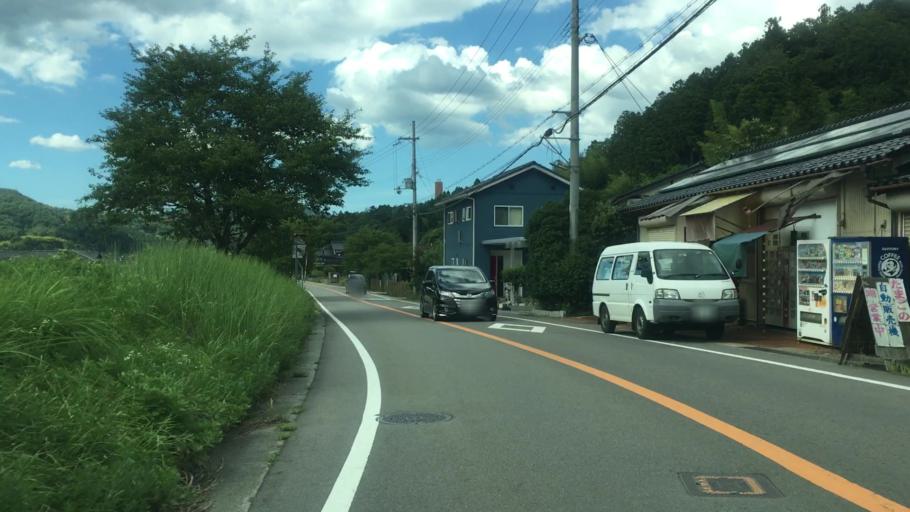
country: JP
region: Hyogo
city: Toyooka
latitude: 35.5402
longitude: 134.7902
